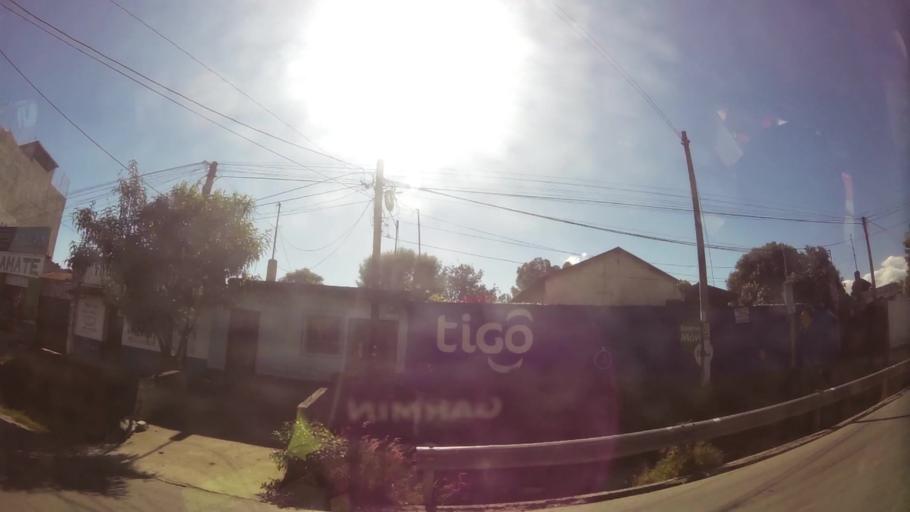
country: GT
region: Guatemala
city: Villa Nueva
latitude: 14.5450
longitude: -90.6172
